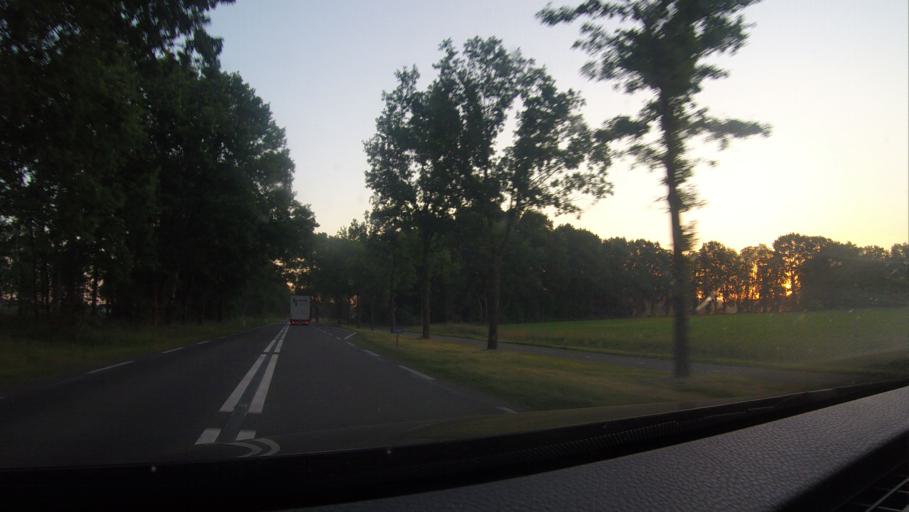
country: NL
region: Overijssel
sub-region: Gemeente Raalte
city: Raalte
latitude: 52.3515
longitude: 6.2726
